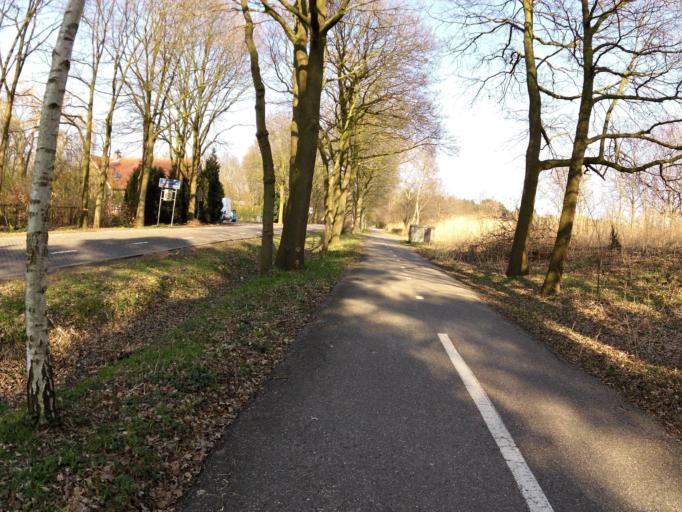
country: NL
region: North Brabant
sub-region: Gemeente Maasdonk
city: Geffen
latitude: 51.7160
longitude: 5.3878
